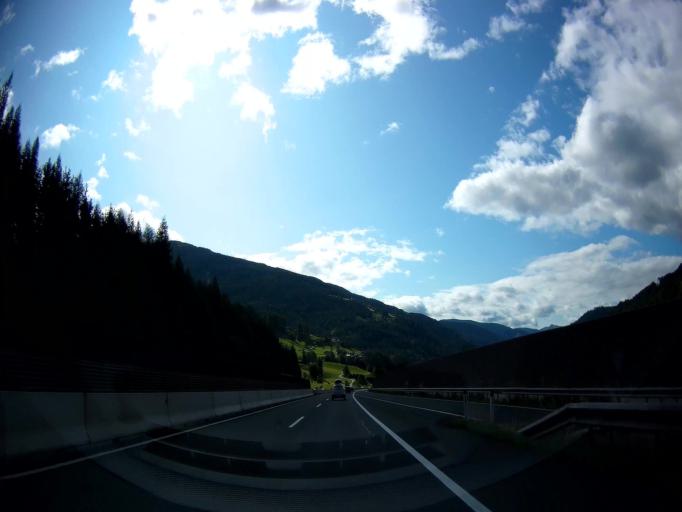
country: AT
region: Salzburg
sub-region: Politischer Bezirk Tamsweg
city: Sankt Michael im Lungau
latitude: 47.0205
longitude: 13.6128
